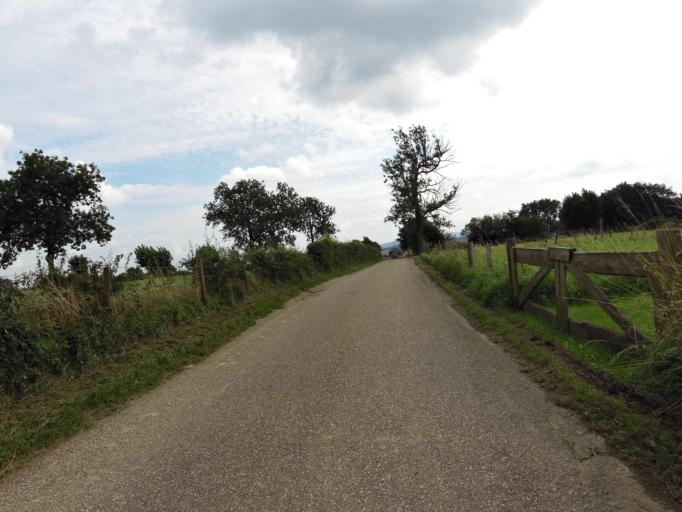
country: NL
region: Limburg
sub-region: Gemeente Voerendaal
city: Ubachsberg
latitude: 50.8402
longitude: 5.9517
